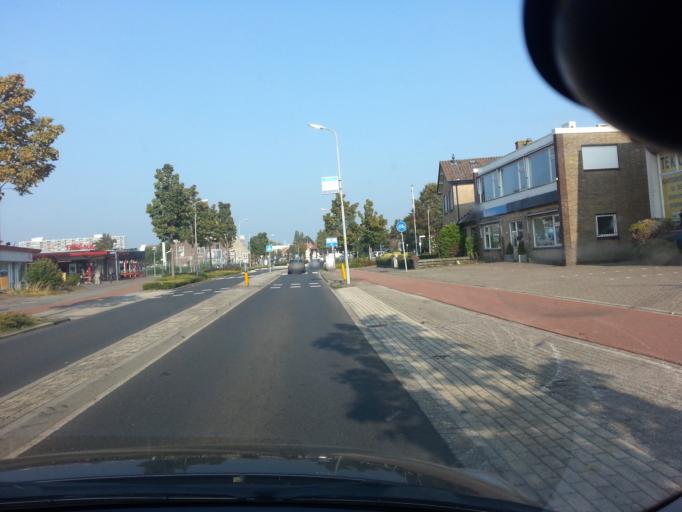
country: NL
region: South Holland
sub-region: Gemeente Zwijndrecht
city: Zwijndrecht
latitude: 51.8186
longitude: 4.6434
